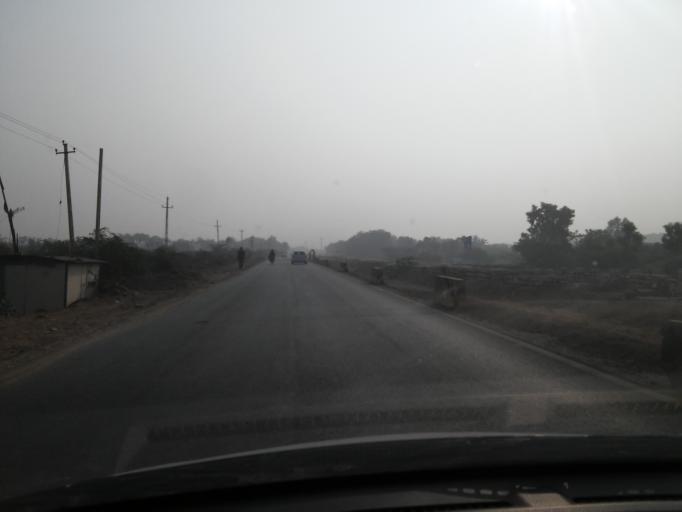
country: IN
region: Gujarat
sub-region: Kachchh
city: Bhuj
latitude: 23.2315
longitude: 69.7512
